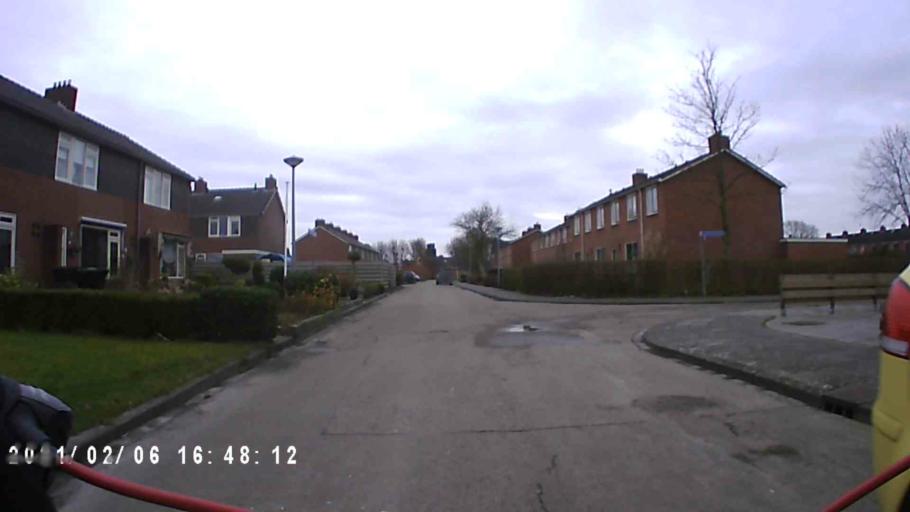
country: NL
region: Groningen
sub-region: Gemeente Appingedam
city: Appingedam
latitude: 53.4153
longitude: 6.7315
